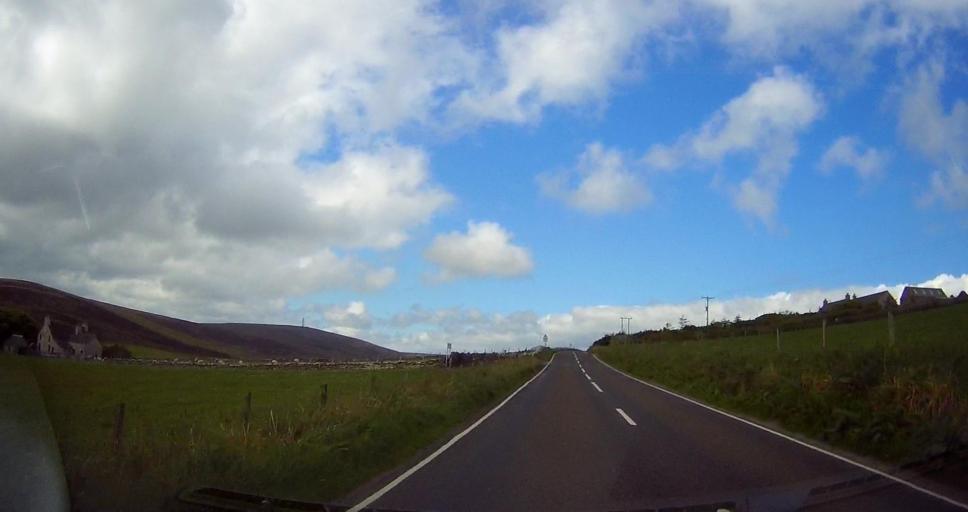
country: GB
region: Scotland
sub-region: Orkney Islands
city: Orkney
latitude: 58.9801
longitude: -3.0314
